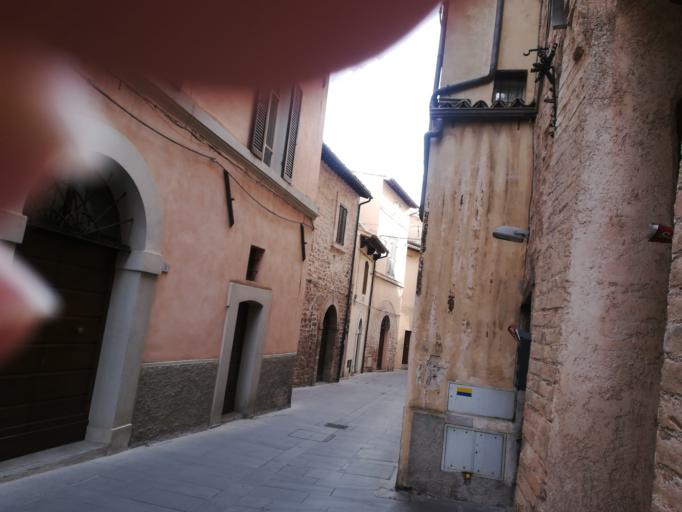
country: IT
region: Umbria
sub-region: Provincia di Perugia
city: Spello
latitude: 42.9933
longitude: 12.6718
